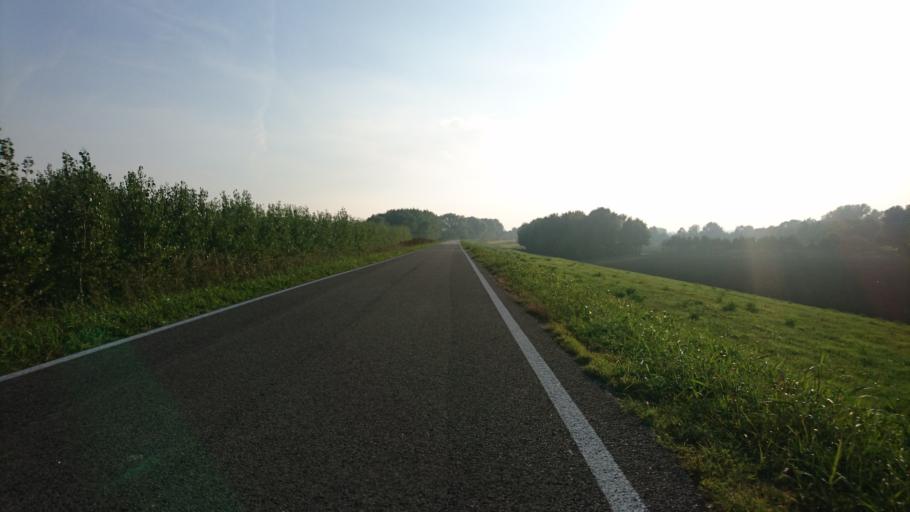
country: IT
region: Emilia-Romagna
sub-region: Provincia di Ferrara
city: Francolino
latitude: 44.9067
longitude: 11.6503
